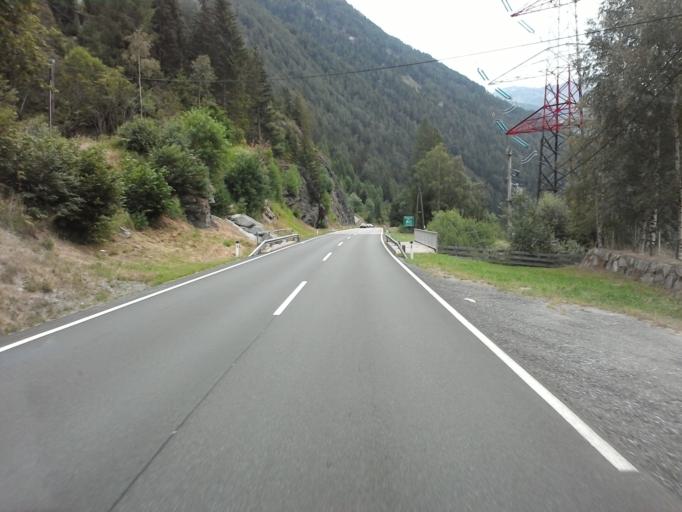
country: AT
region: Tyrol
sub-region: Politischer Bezirk Lienz
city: Matrei in Osttirol
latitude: 47.0240
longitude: 12.5274
